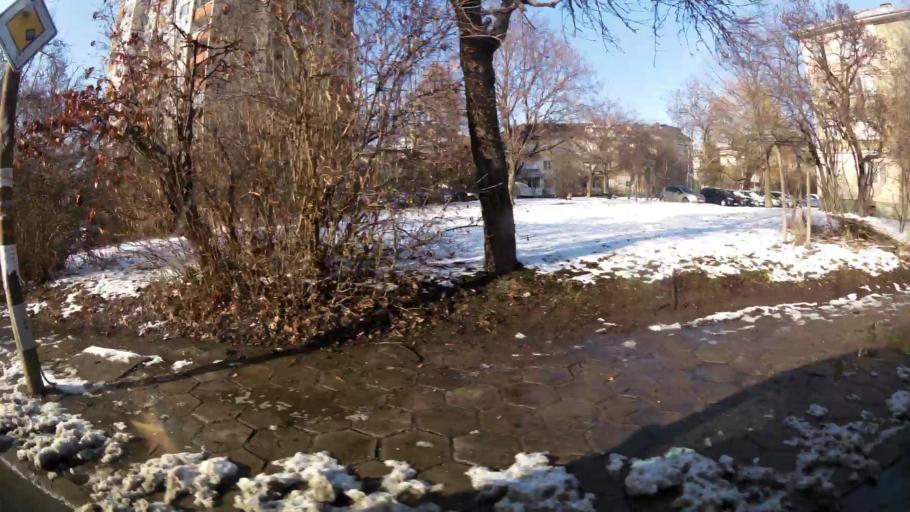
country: BG
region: Sofia-Capital
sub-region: Stolichna Obshtina
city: Sofia
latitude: 42.6685
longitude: 23.3610
